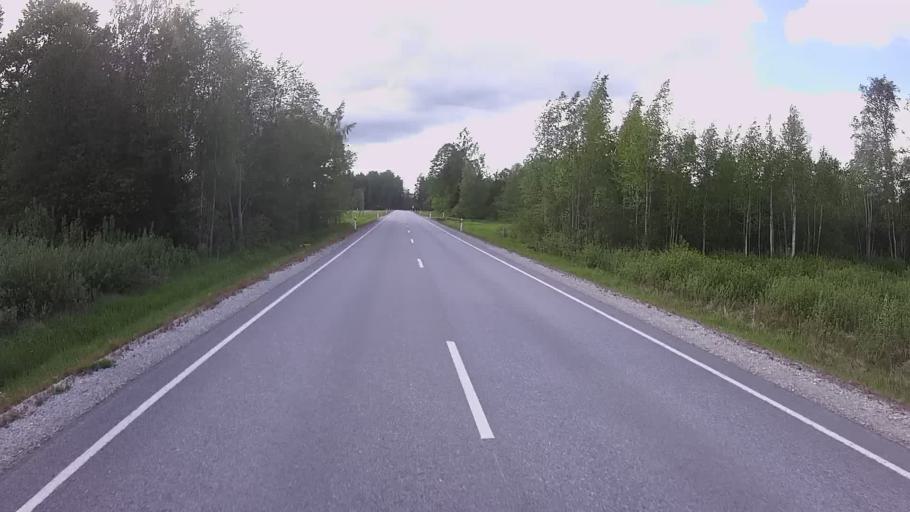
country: EE
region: Jogevamaa
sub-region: Mustvee linn
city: Mustvee
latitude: 58.8681
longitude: 26.8332
